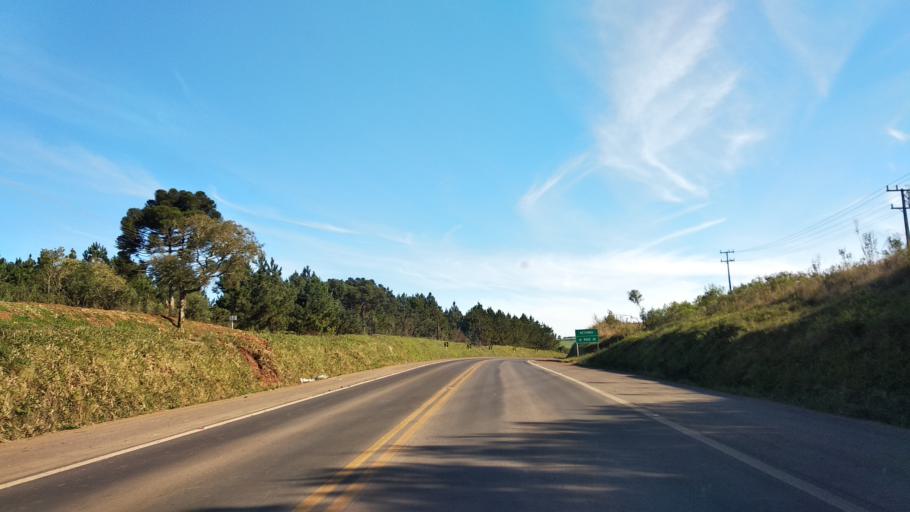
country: BR
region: Santa Catarina
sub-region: Campos Novos
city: Campos Novos
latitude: -27.4066
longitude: -51.2081
